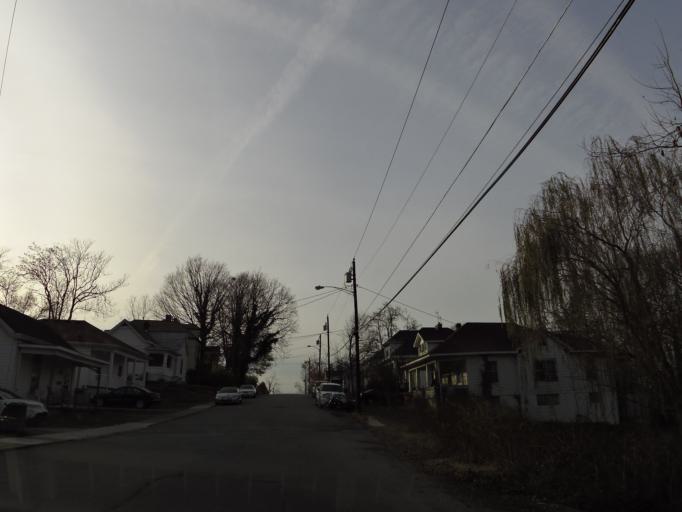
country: US
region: Kentucky
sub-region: Harrison County
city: Cynthiana
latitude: 38.3898
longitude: -84.2896
